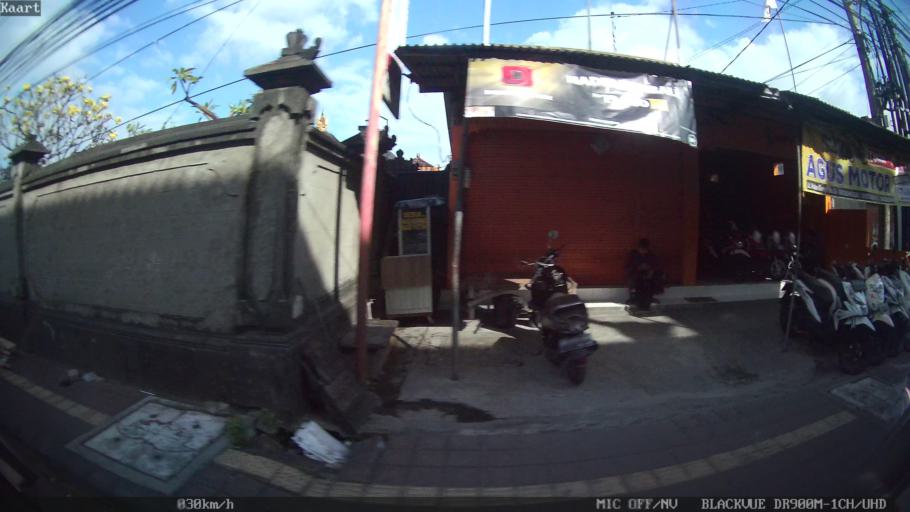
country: ID
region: Bali
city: Karyadharma
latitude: -8.6887
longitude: 115.2062
